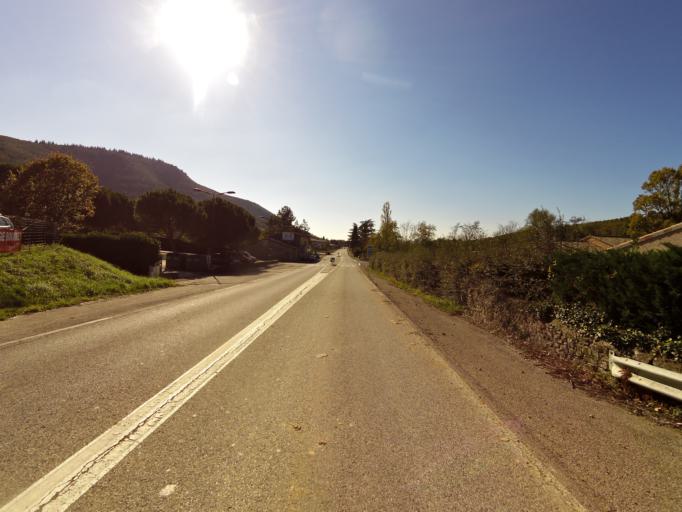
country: FR
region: Rhone-Alpes
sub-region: Departement de l'Ardeche
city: Vesseaux
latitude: 44.6495
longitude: 4.4407
